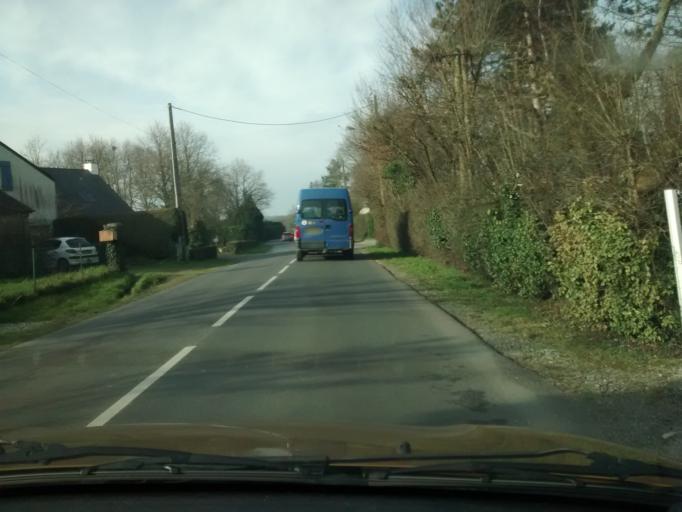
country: FR
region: Pays de la Loire
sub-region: Departement de la Loire-Atlantique
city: Notre-Dame-des-Landes
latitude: 47.3801
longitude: -1.7125
